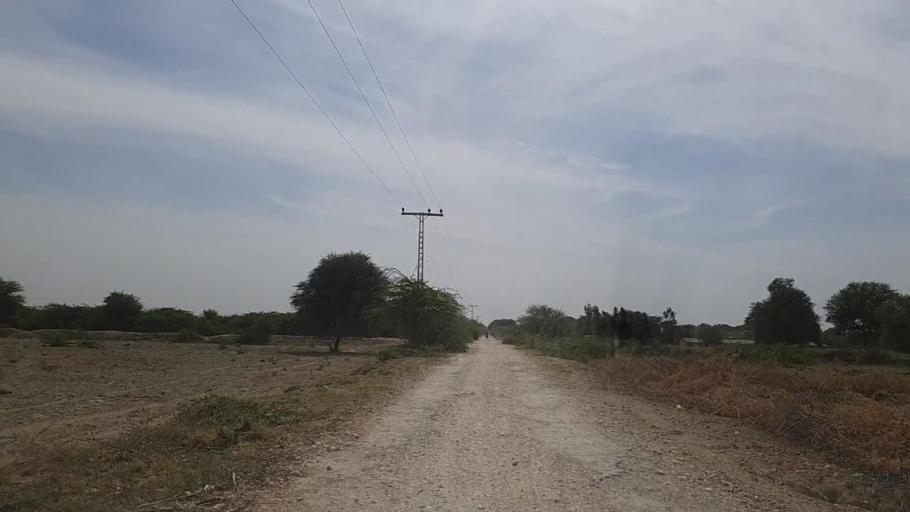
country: PK
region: Sindh
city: Samaro
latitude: 25.2604
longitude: 69.4535
